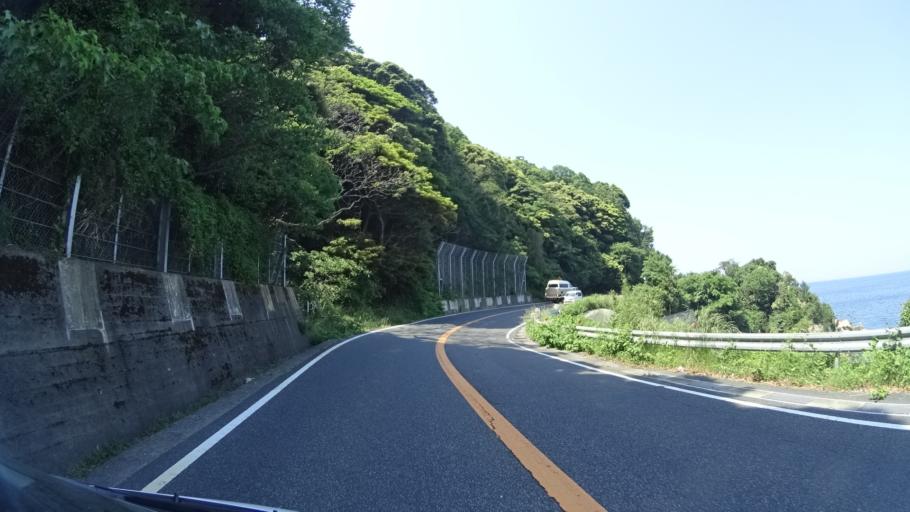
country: JP
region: Kyoto
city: Miyazu
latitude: 35.5311
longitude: 135.2691
